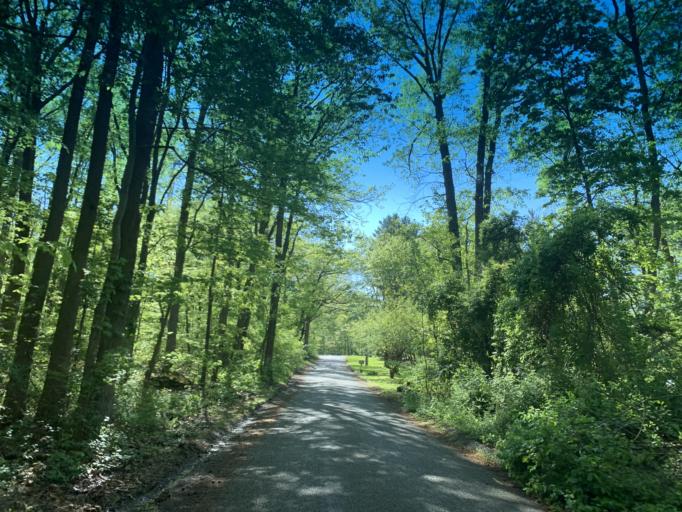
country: US
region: Maryland
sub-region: Harford County
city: Riverside
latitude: 39.4520
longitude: -76.2648
